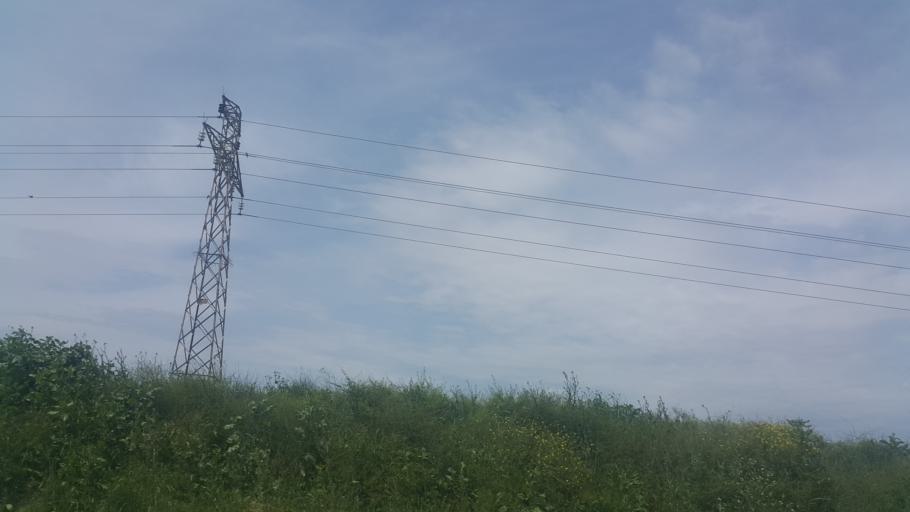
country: TR
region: Adana
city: Yakapinar
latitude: 36.9898
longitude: 35.6682
